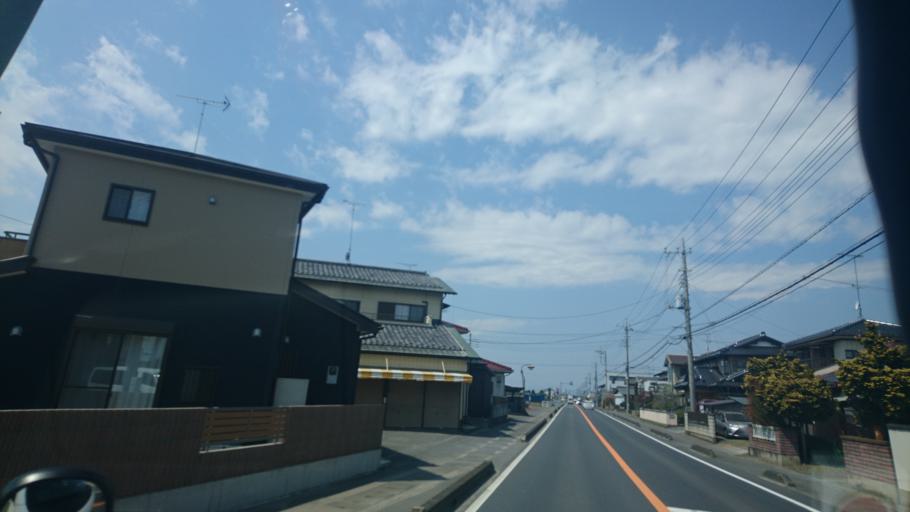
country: JP
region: Ibaraki
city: Yuki
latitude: 36.2795
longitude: 139.9034
